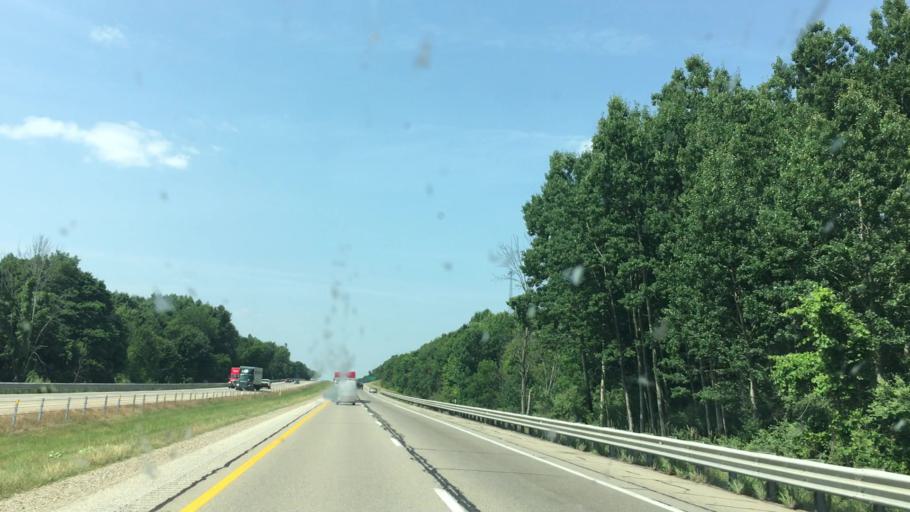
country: US
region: Michigan
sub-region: Allegan County
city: Wayland
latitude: 42.5700
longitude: -85.6623
